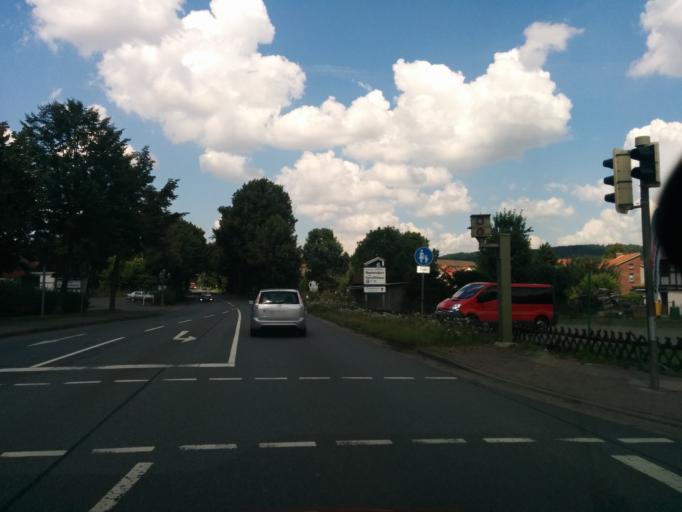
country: DE
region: Lower Saxony
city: Gieboldehausen
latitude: 51.6099
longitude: 10.2111
